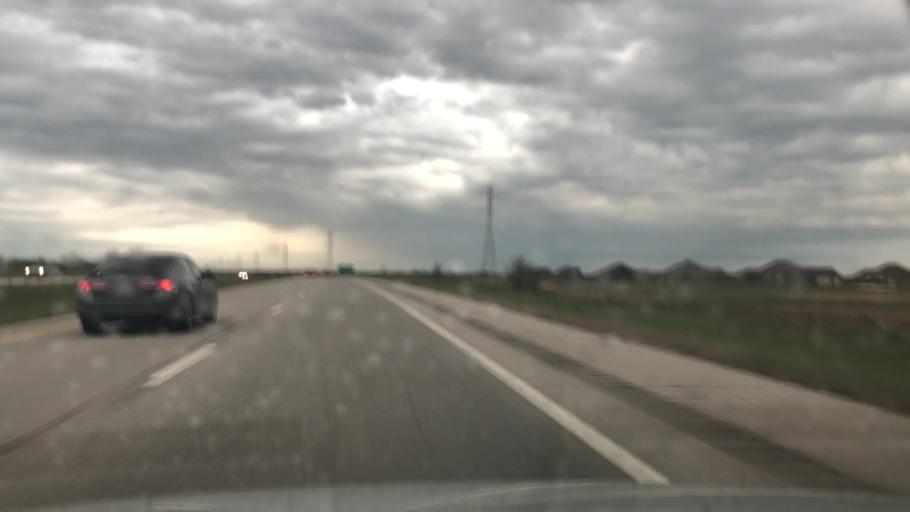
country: US
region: Oklahoma
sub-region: Tulsa County
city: Sperry
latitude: 36.3430
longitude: -95.9235
